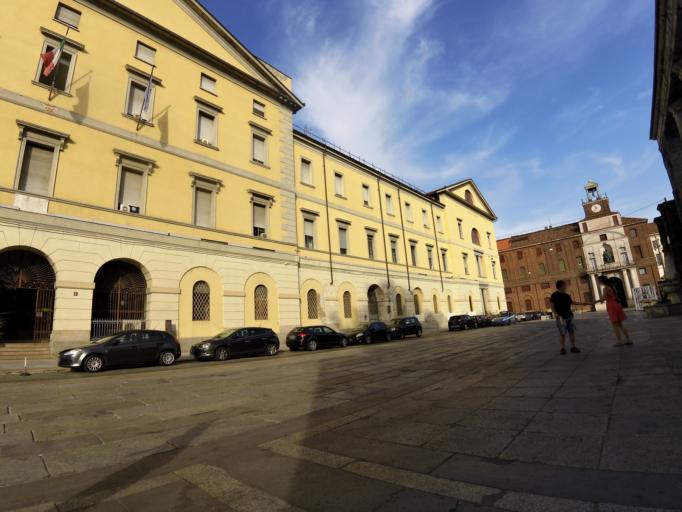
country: IT
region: Lombardy
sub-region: Citta metropolitana di Milano
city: Milano
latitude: 45.4635
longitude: 9.1760
